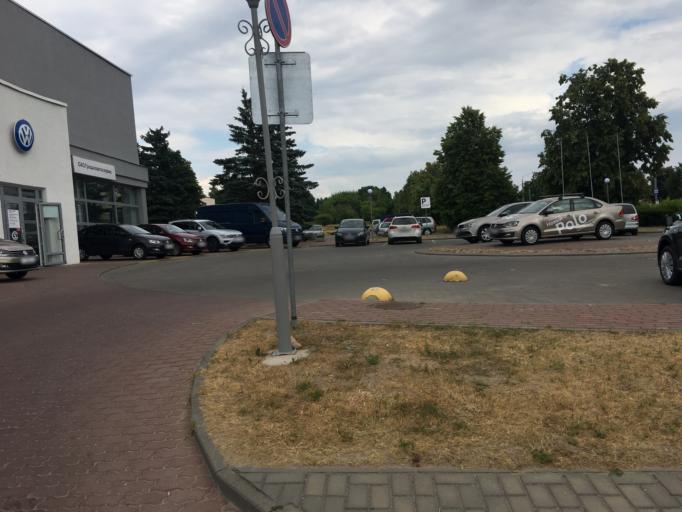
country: BY
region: Grodnenskaya
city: Hrodna
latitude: 53.6734
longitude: 23.8720
